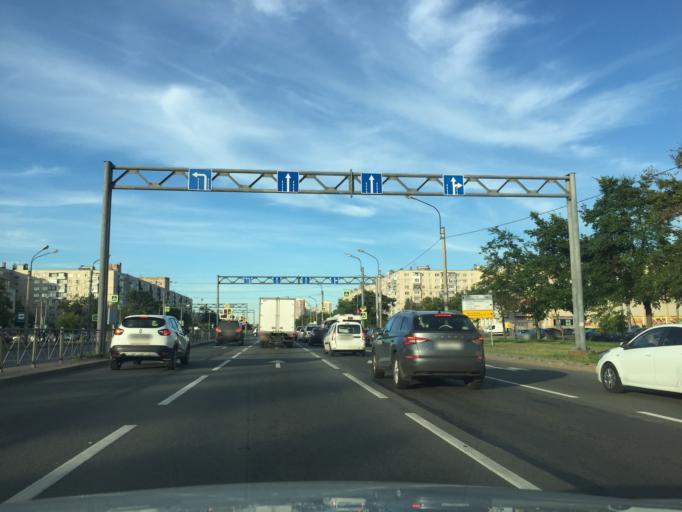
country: RU
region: St.-Petersburg
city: Shushary
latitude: 59.8383
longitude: 30.3948
